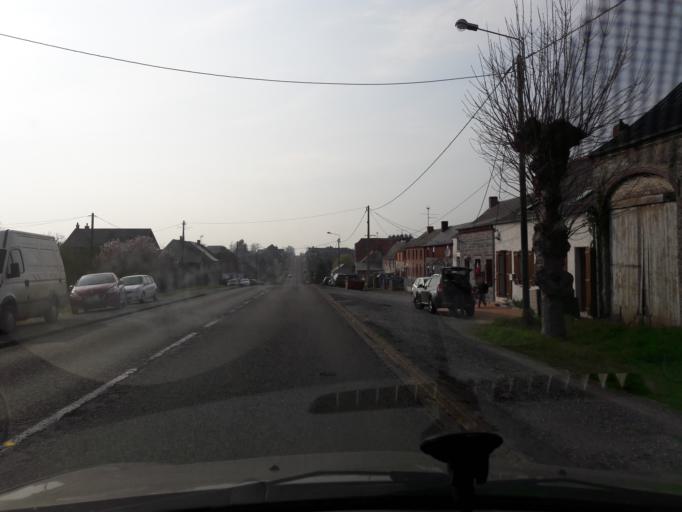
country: FR
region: Nord-Pas-de-Calais
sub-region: Departement du Nord
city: Marpent
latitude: 50.2533
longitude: 4.0821
